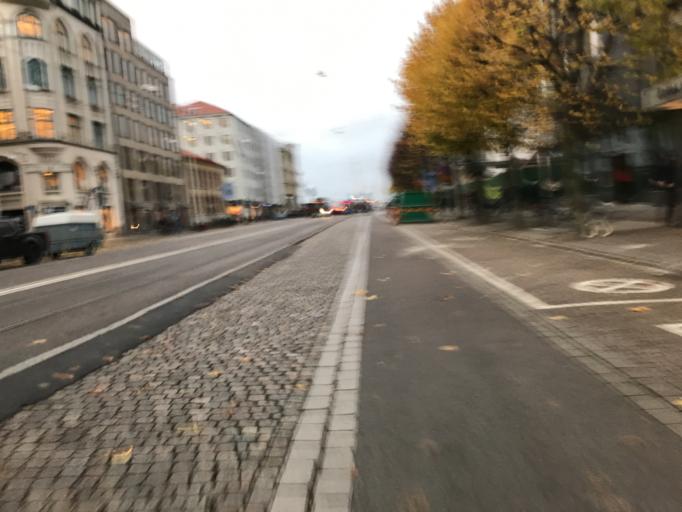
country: SE
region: Vaestra Goetaland
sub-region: Goteborg
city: Goeteborg
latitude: 57.7081
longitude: 11.9674
